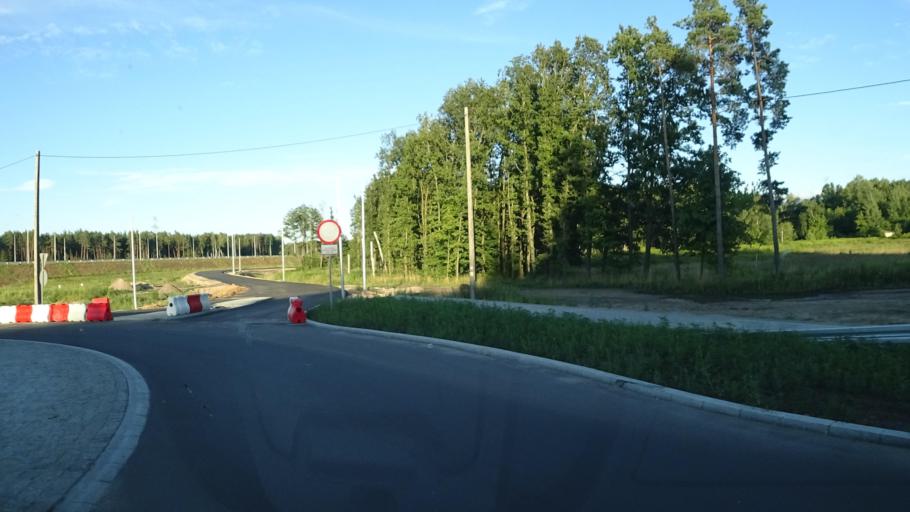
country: PL
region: Warmian-Masurian Voivodeship
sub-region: Powiat elcki
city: Elk
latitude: 53.8373
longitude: 22.4155
